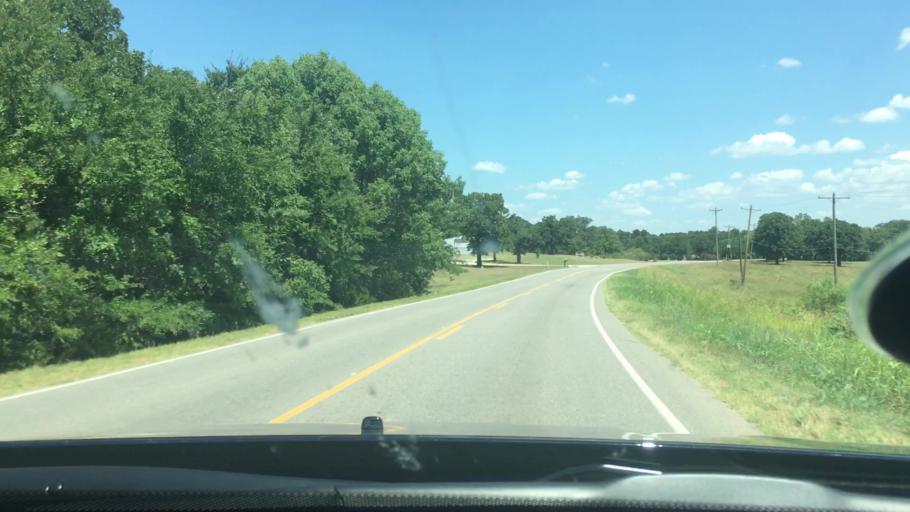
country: US
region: Oklahoma
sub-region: Carter County
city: Dickson
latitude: 34.1919
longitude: -96.9858
